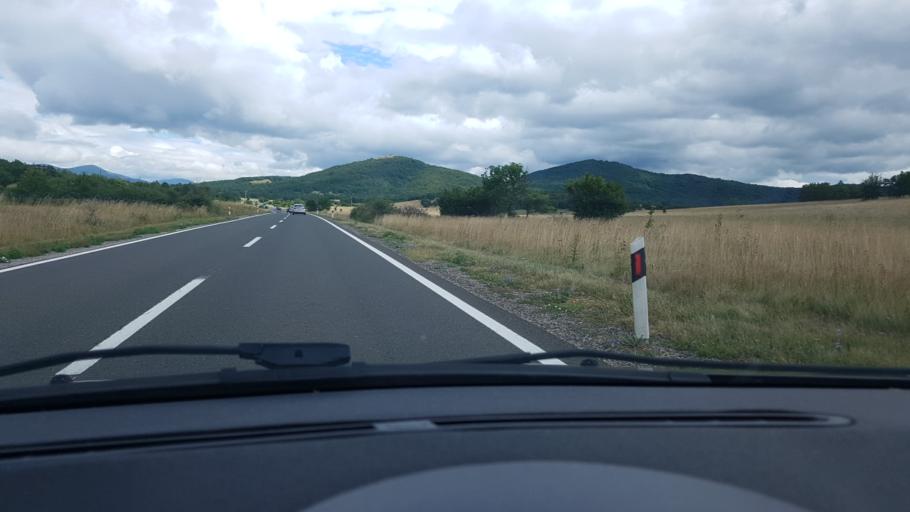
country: HR
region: Zadarska
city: Gracac
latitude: 44.4678
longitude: 15.7983
